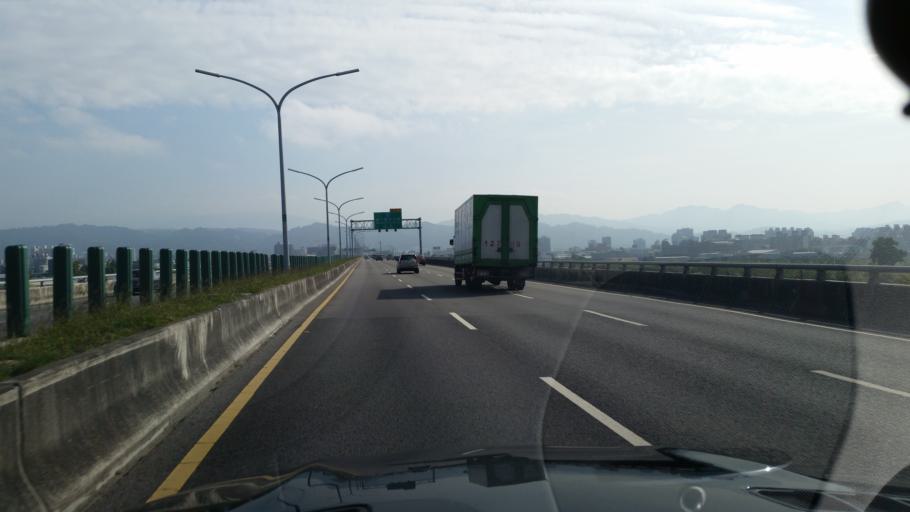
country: TW
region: Taiwan
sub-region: Taichung City
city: Taichung
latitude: 24.2010
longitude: 120.6861
